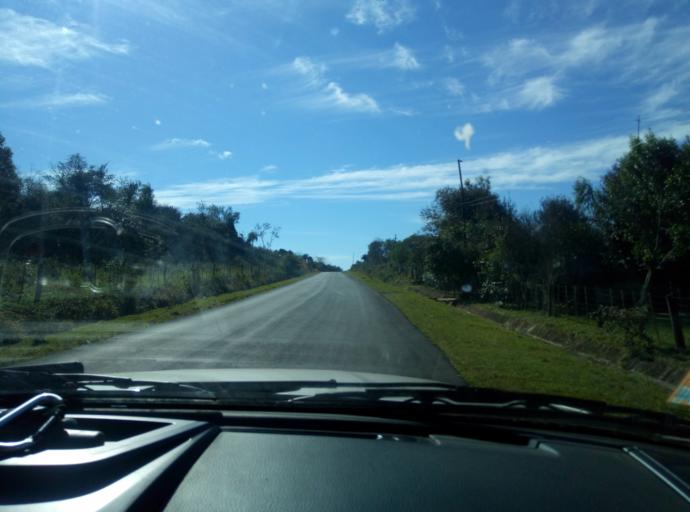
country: PY
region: Caaguazu
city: Carayao
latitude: -25.1706
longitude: -56.3129
